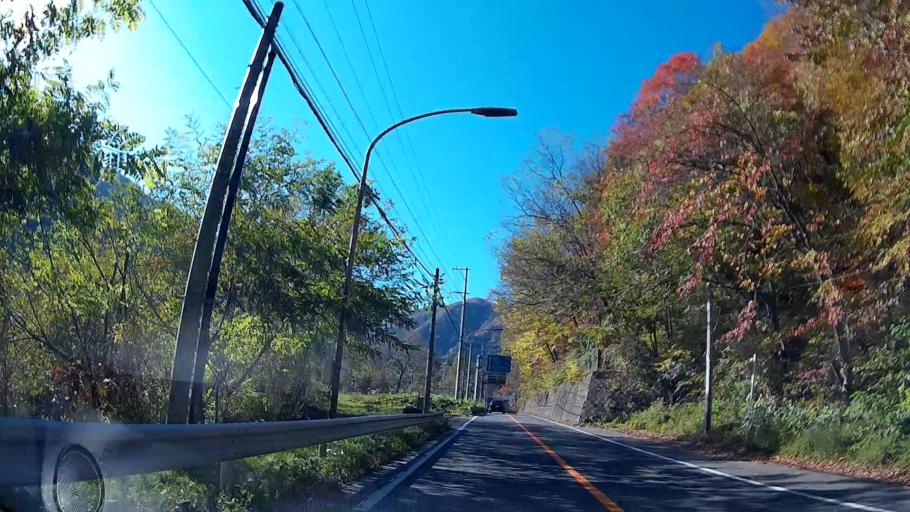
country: JP
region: Nagano
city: Toyoshina
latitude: 36.1463
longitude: 137.6915
